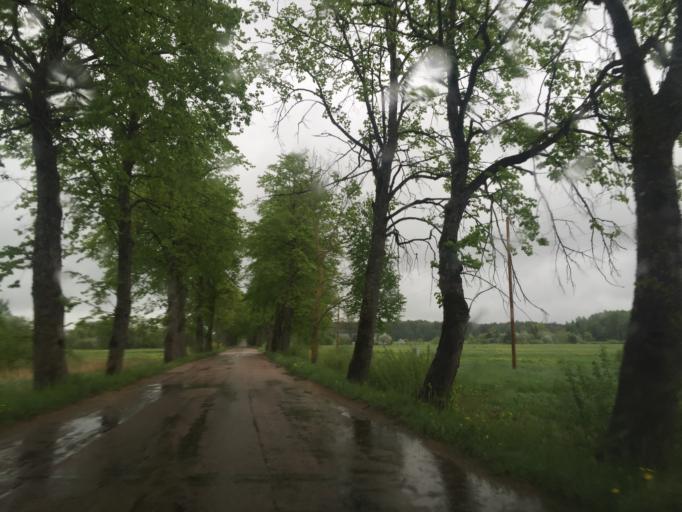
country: LV
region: Ogre
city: Jumprava
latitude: 56.6448
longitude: 24.9206
